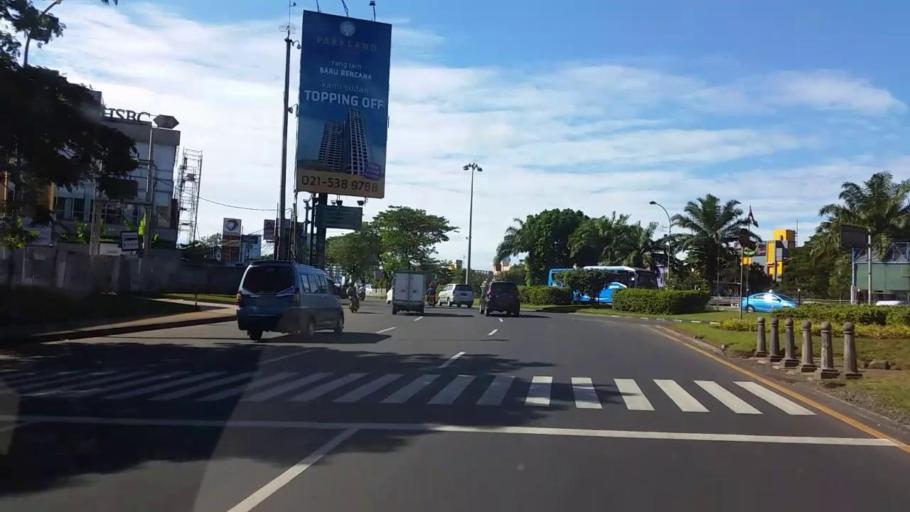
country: ID
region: West Java
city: Serpong
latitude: -6.2864
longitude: 106.6656
